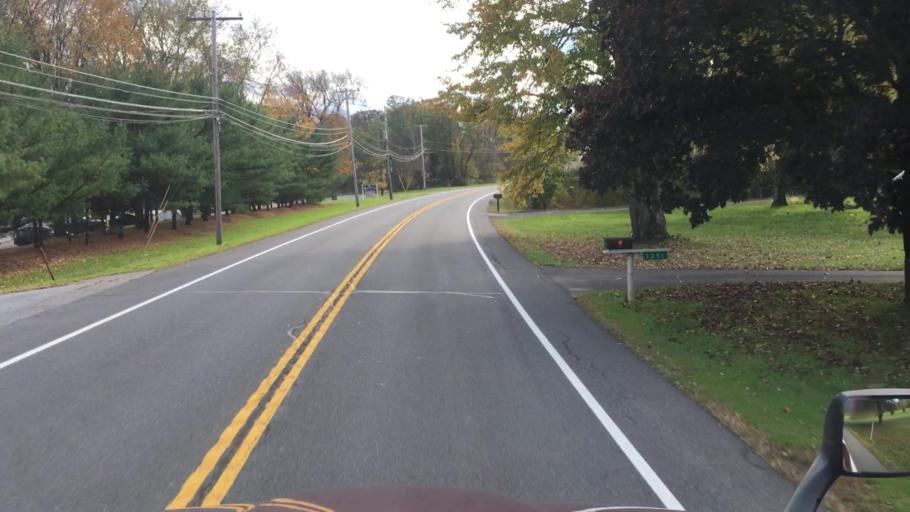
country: US
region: New York
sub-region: Saratoga County
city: Ballston Spa
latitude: 42.9633
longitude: -73.8634
